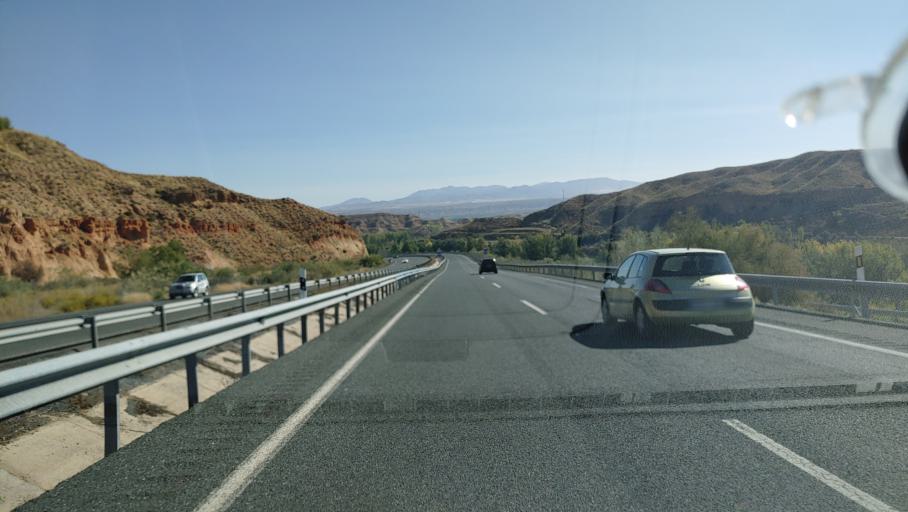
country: ES
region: Andalusia
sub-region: Provincia de Granada
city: Marchal
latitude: 37.3274
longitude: -3.2324
